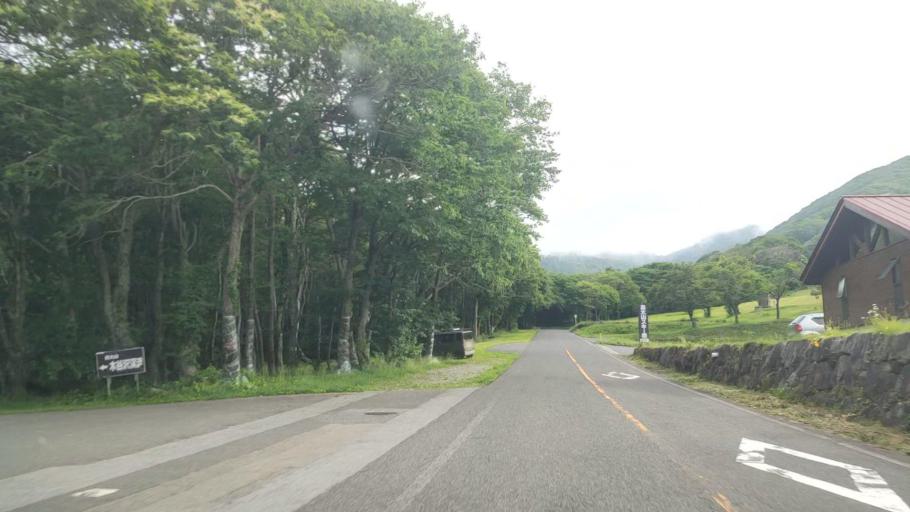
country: JP
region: Tottori
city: Yonago
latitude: 35.3390
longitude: 133.5557
